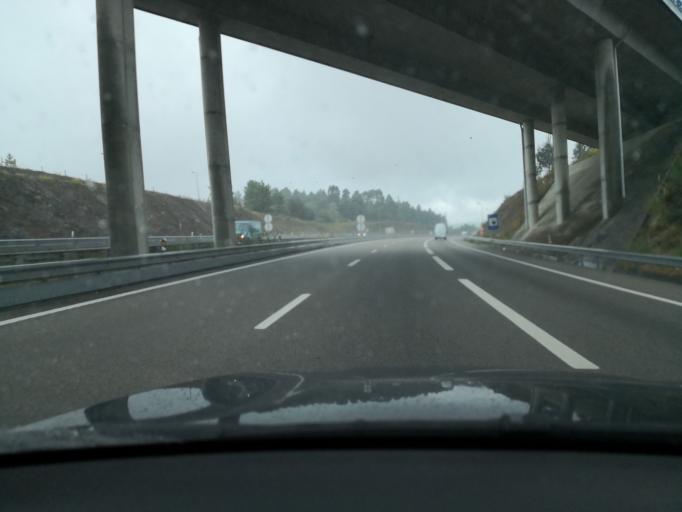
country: PT
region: Porto
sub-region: Pacos de Ferreira
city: Seroa
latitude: 41.2468
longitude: -8.4352
